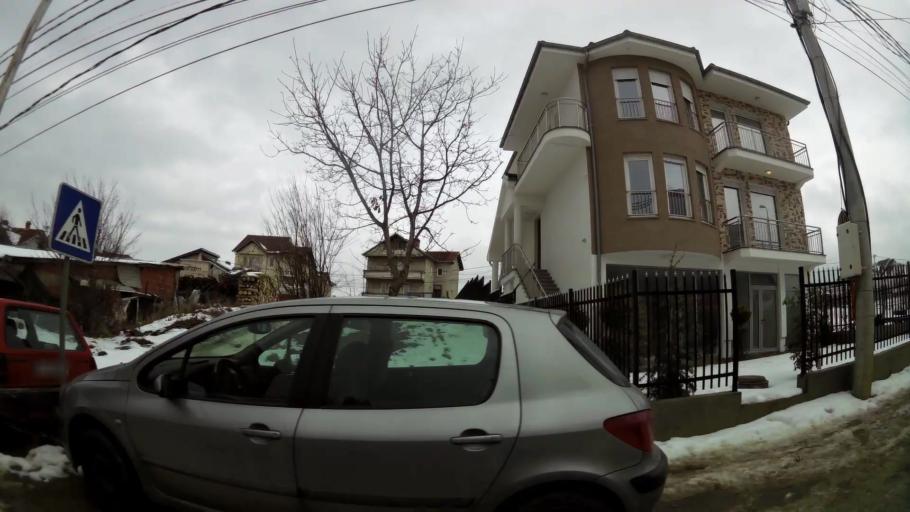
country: XK
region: Pristina
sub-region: Komuna e Prishtines
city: Pristina
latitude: 42.6575
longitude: 21.1859
